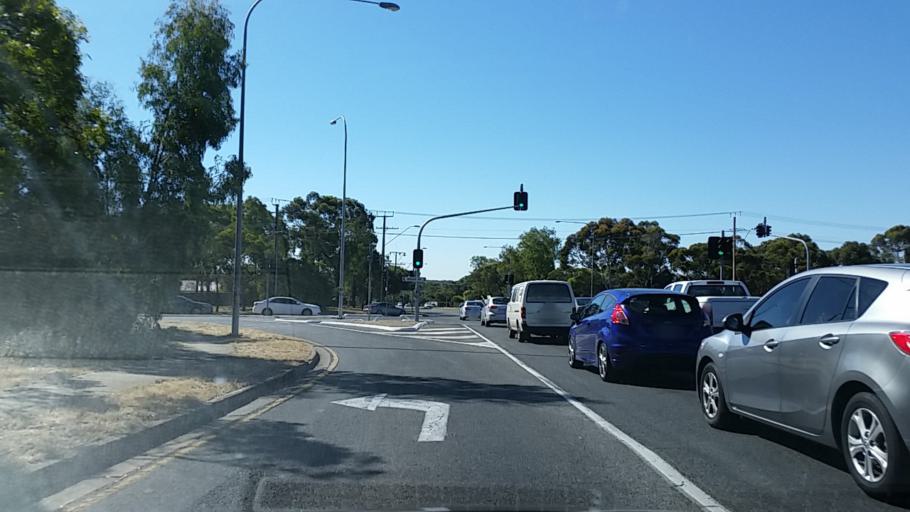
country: AU
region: South Australia
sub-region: Salisbury
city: Salisbury
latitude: -34.7984
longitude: 138.6575
